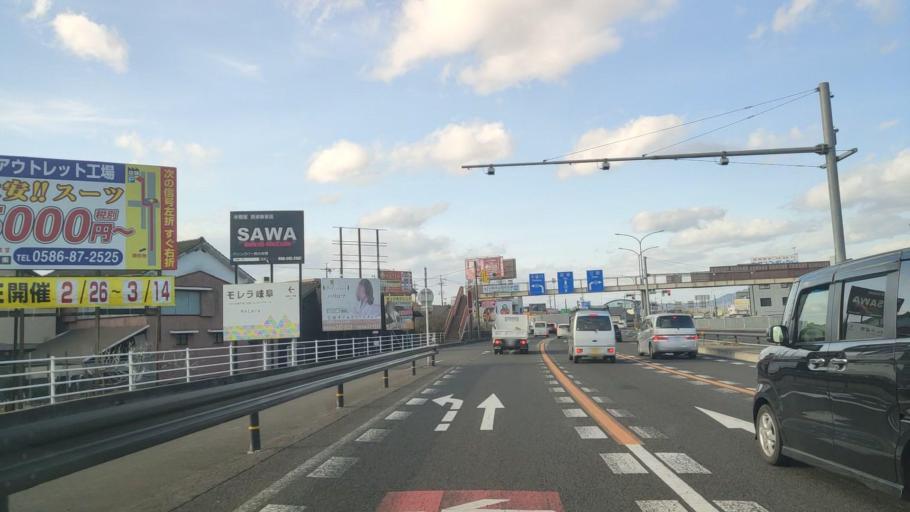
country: JP
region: Aichi
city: Kuroda
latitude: 35.3604
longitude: 136.7830
